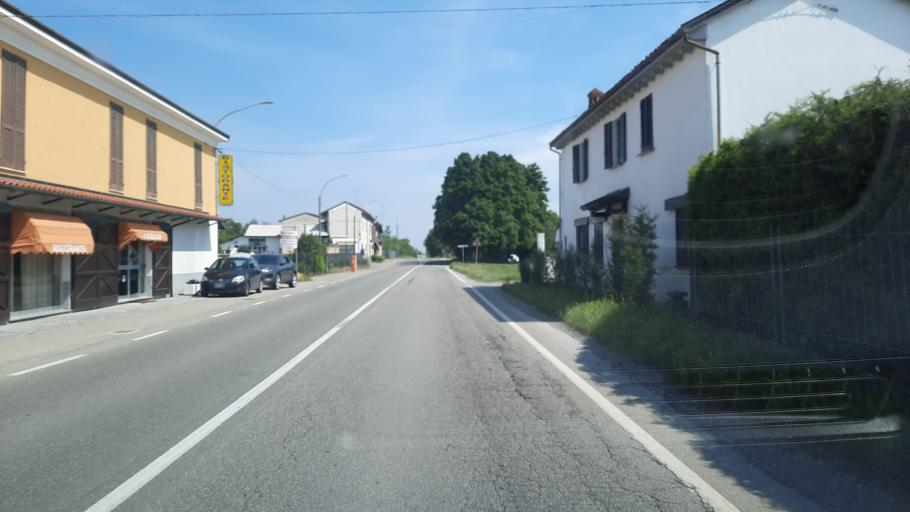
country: IT
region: Lombardy
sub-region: Provincia di Pavia
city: Cergnago
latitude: 45.2349
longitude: 8.7996
